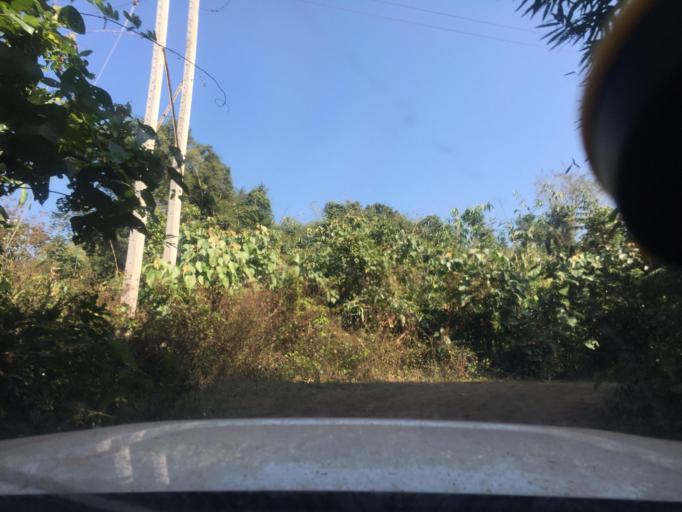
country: LA
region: Phongsali
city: Phongsali
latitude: 21.6860
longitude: 102.4103
